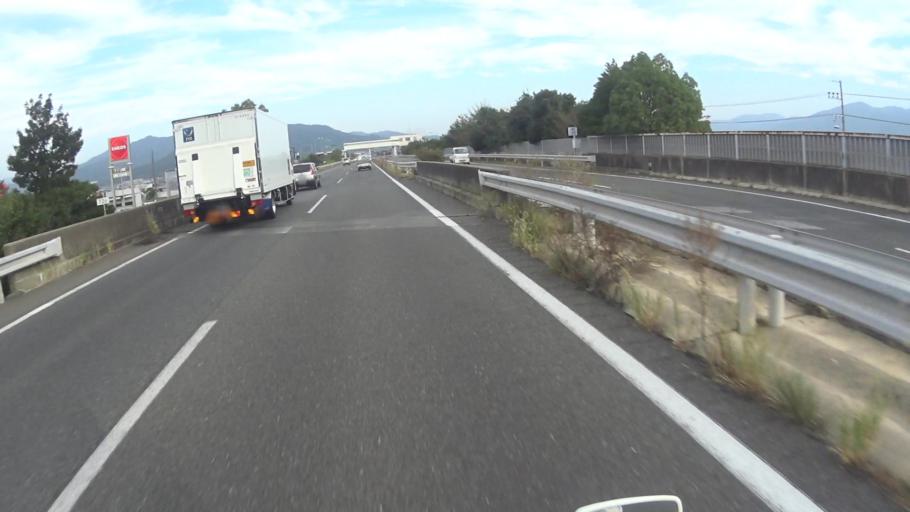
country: JP
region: Kyoto
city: Kameoka
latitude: 35.0126
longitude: 135.5578
